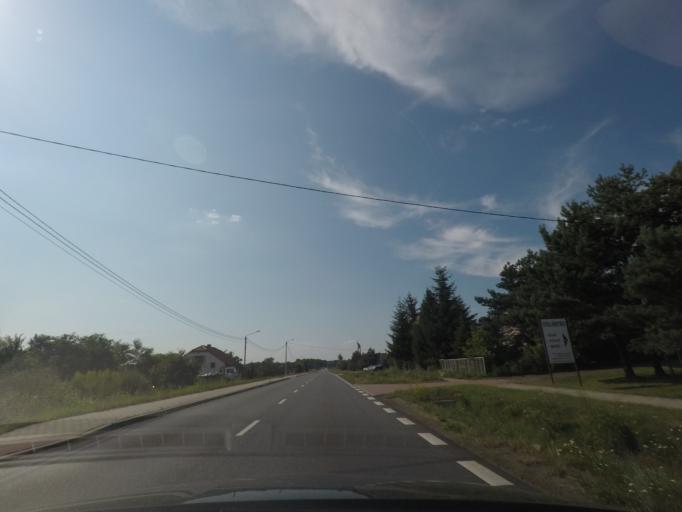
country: PL
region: Silesian Voivodeship
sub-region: Powiat pszczynski
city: Radostowice
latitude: 50.0103
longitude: 18.8625
